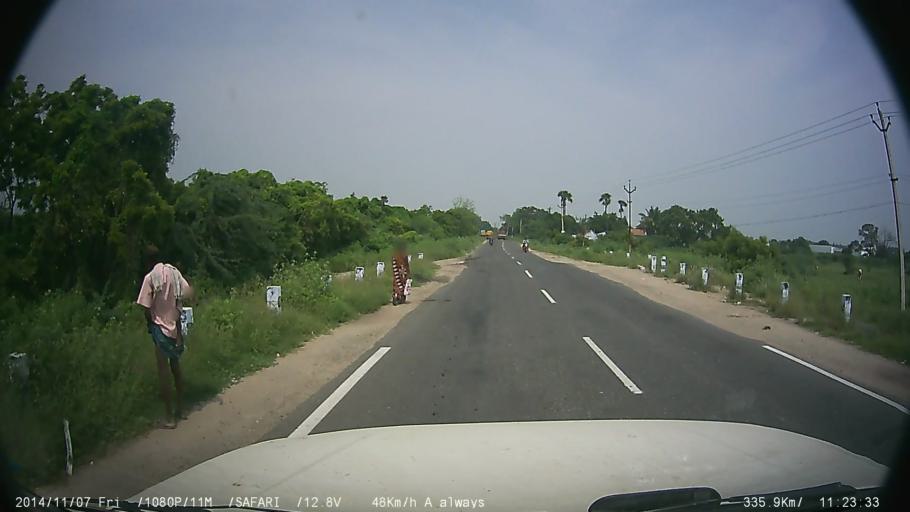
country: IN
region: Tamil Nadu
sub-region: Tiruppur
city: Avinashi
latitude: 11.1100
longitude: 77.2711
